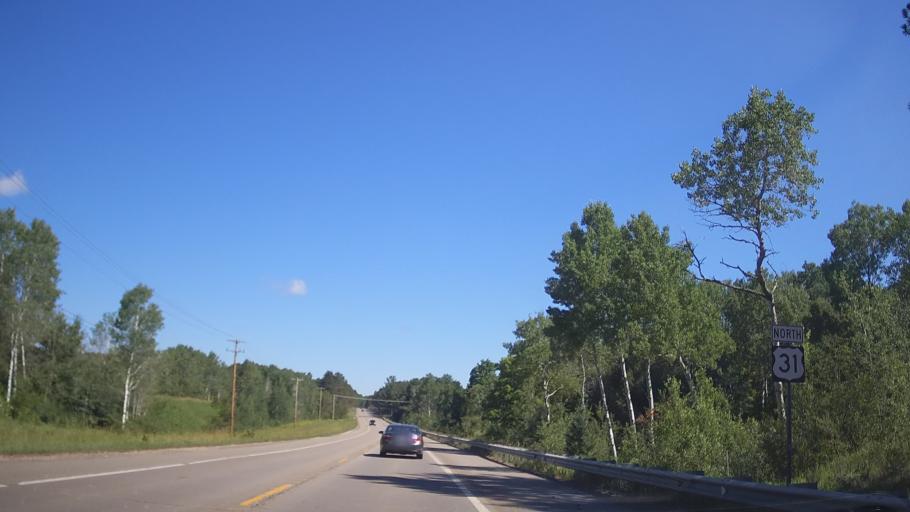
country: US
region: Michigan
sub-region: Cheboygan County
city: Indian River
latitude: 45.5365
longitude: -84.7822
